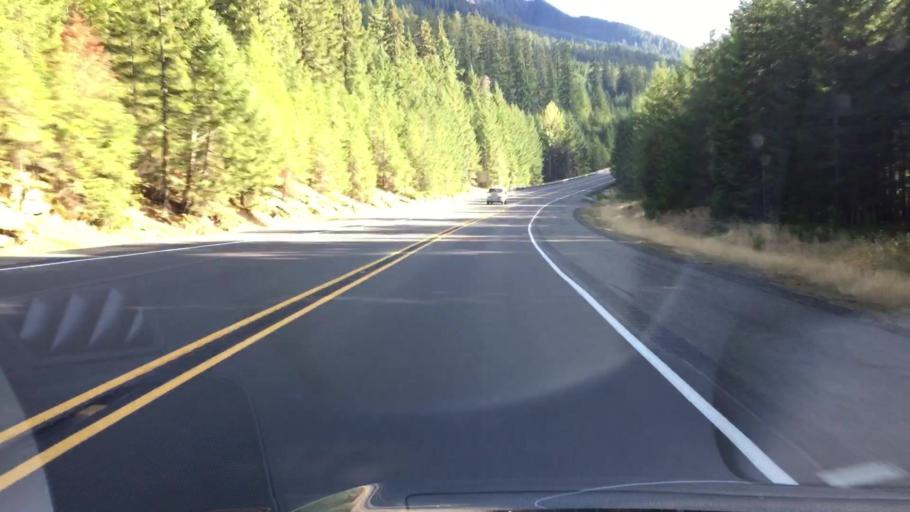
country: US
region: Washington
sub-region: Pierce County
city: Buckley
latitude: 46.6817
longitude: -121.5749
